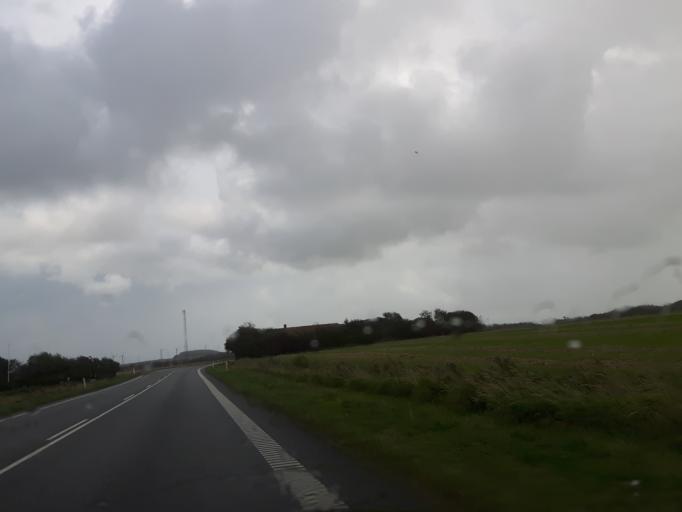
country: DK
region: North Denmark
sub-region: Thisted Kommune
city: Hurup
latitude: 56.6502
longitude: 8.4675
